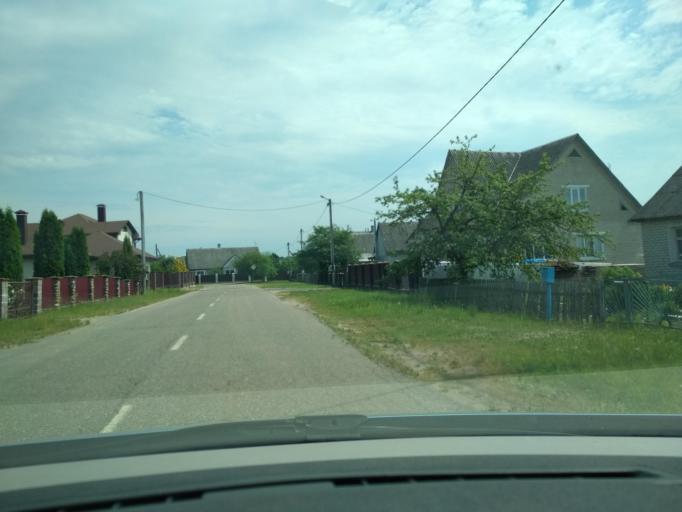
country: BY
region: Grodnenskaya
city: Astravyets
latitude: 54.6204
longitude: 25.9554
